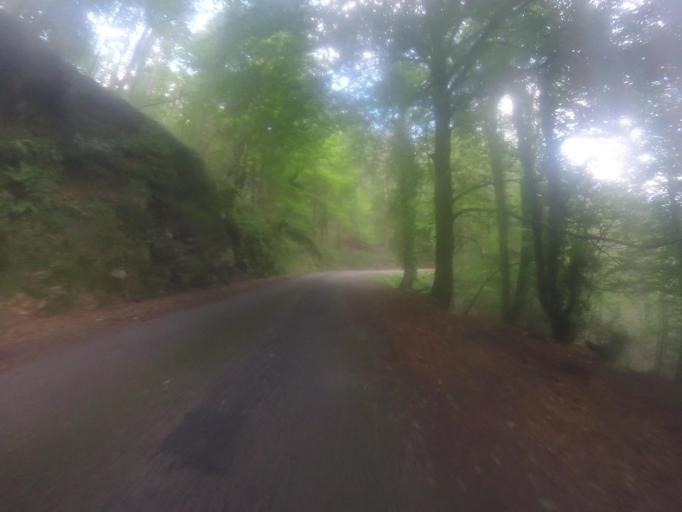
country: ES
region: Navarre
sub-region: Provincia de Navarra
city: Goizueta
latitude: 43.2242
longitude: -1.8024
